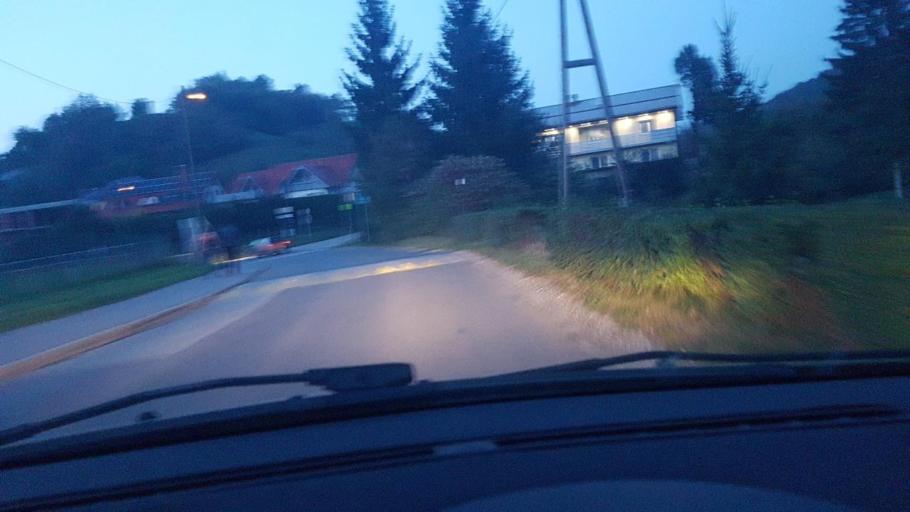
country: SI
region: Maribor
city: Kamnica
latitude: 46.5730
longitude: 15.6242
